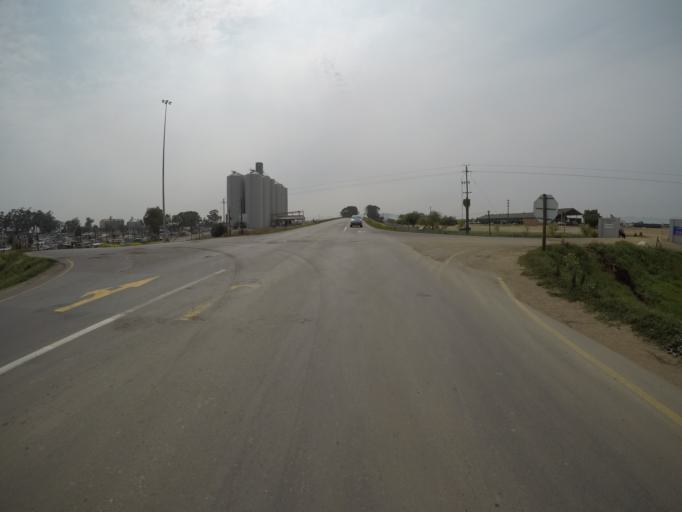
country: ZA
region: Western Cape
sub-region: City of Cape Town
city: Kraaifontein
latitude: -33.7050
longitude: 18.7008
